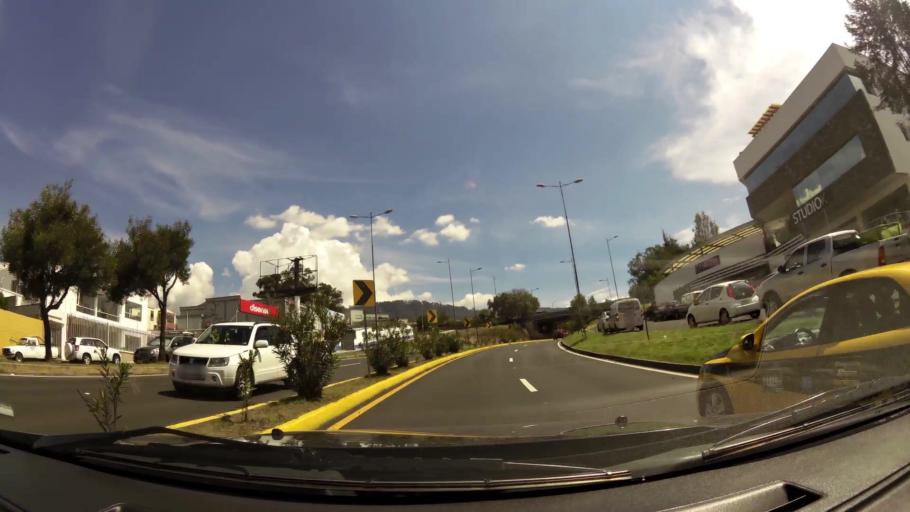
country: EC
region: Pichincha
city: Quito
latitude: -0.2033
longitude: -78.4379
